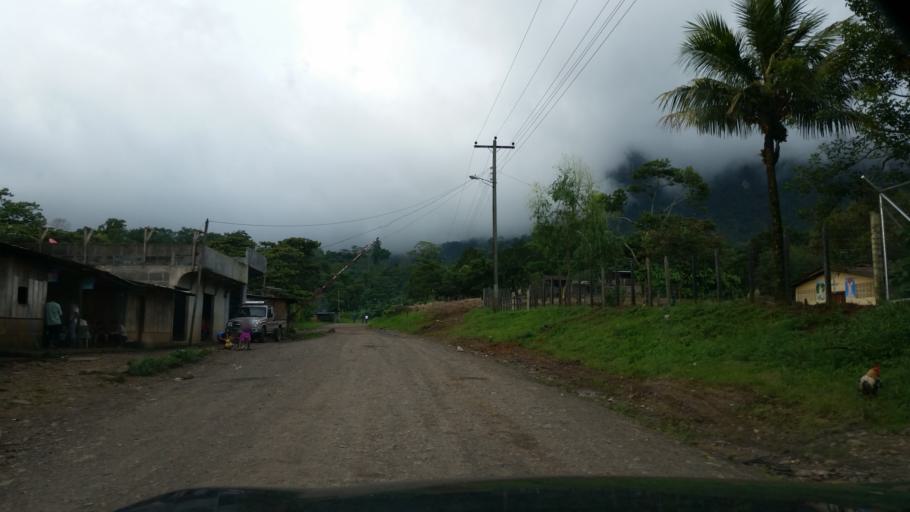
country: NI
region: Jinotega
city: Jinotega
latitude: 13.2731
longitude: -85.7305
